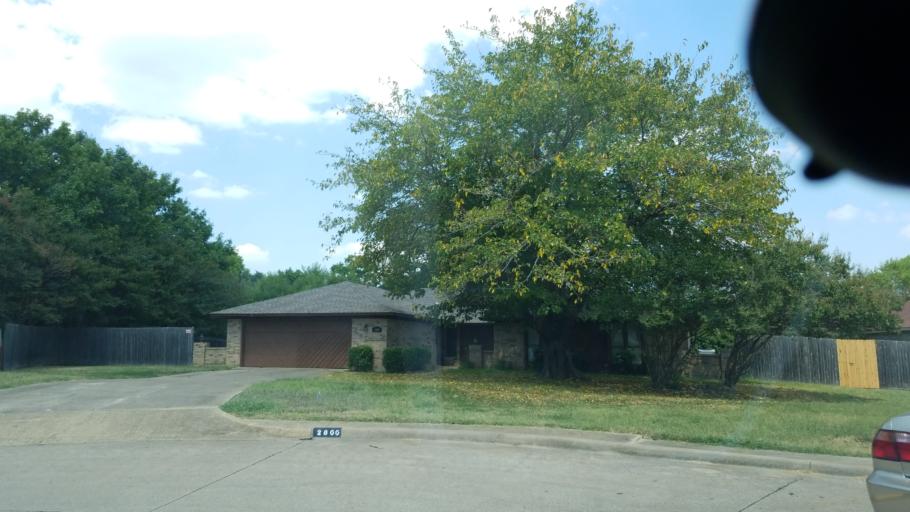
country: US
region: Texas
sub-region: Dallas County
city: Grand Prairie
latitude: 32.7032
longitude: -96.9920
